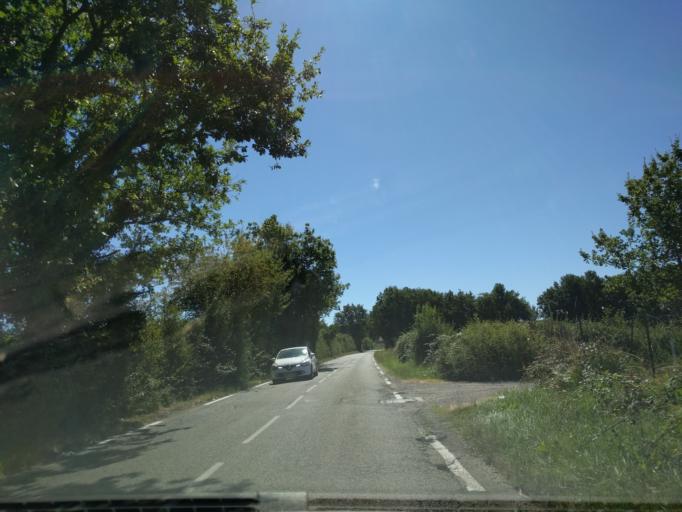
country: FR
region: Midi-Pyrenees
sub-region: Departement du Tarn-et-Garonne
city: Montauban
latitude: 44.0230
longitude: 1.3852
